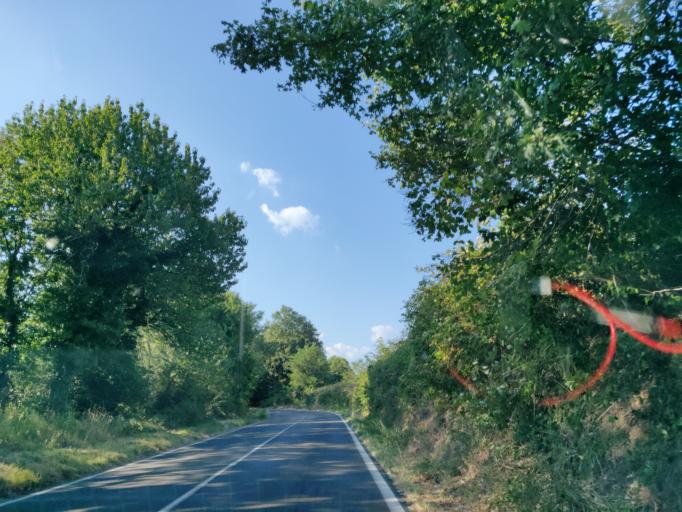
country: IT
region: Latium
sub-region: Provincia di Viterbo
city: Latera
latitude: 42.6207
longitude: 11.8392
